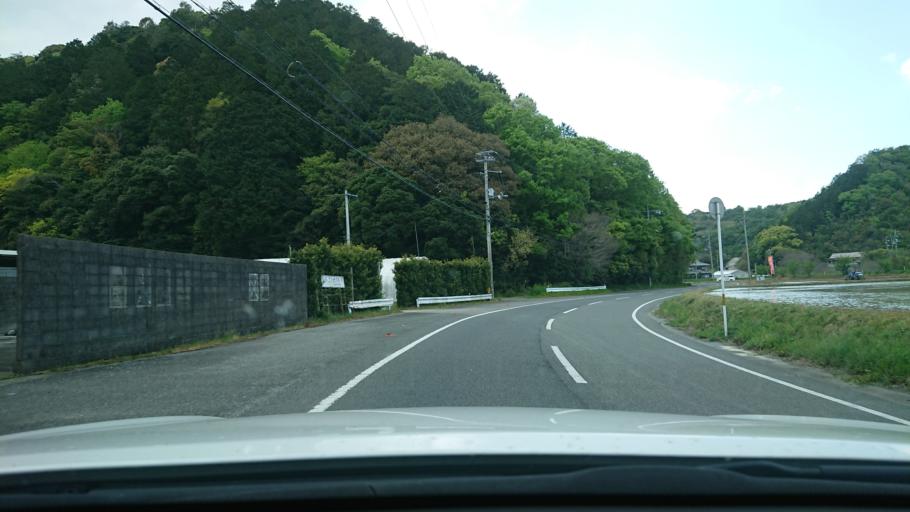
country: JP
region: Tokushima
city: Komatsushimacho
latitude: 33.9812
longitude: 134.5455
